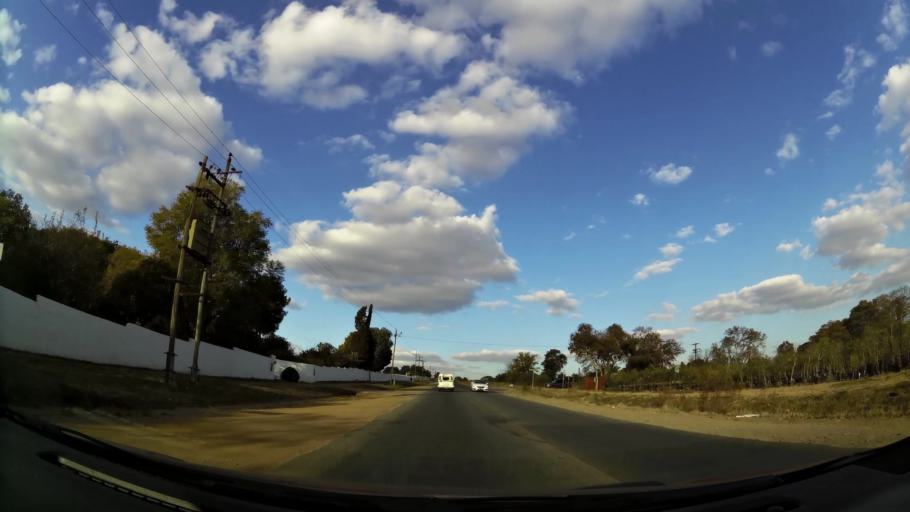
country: ZA
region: Gauteng
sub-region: City of Johannesburg Metropolitan Municipality
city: Midrand
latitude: -25.9563
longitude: 28.1476
